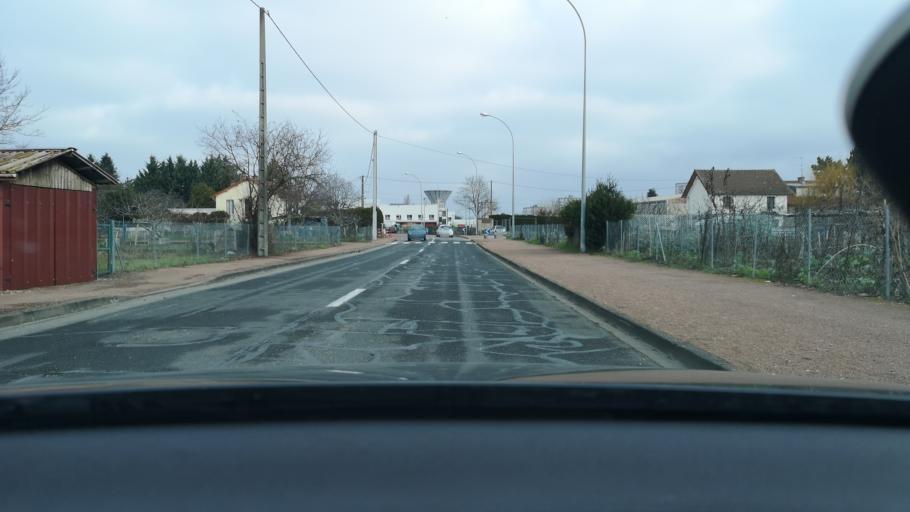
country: FR
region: Bourgogne
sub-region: Departement de Saone-et-Loire
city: Chalon-sur-Saone
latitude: 46.8003
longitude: 4.8502
